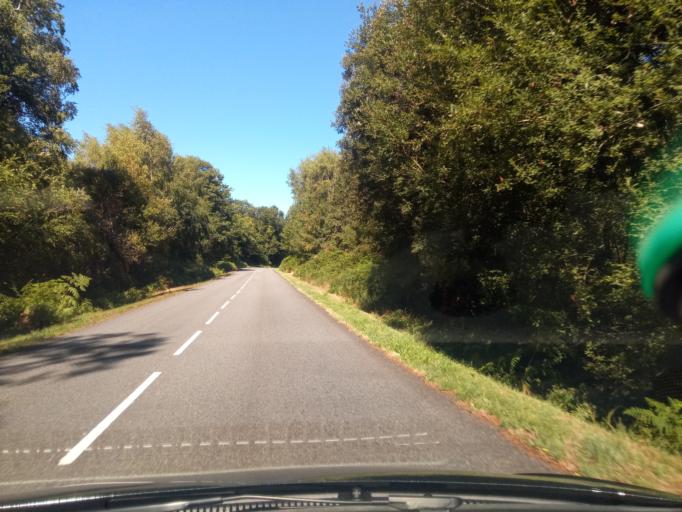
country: FR
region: Limousin
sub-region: Departement de la Haute-Vienne
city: Nantiat
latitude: 46.0668
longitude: 1.2047
